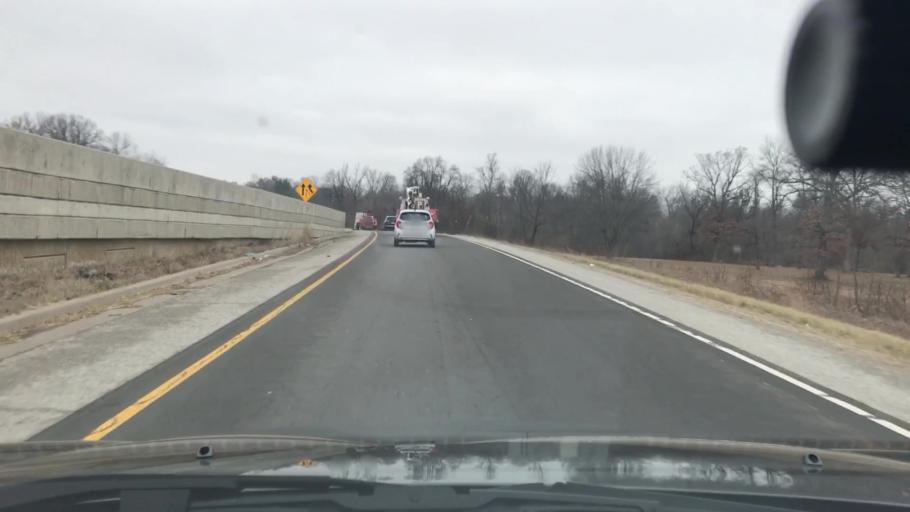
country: US
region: Illinois
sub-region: Madison County
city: Rosewood Heights
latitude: 38.9005
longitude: -90.0659
